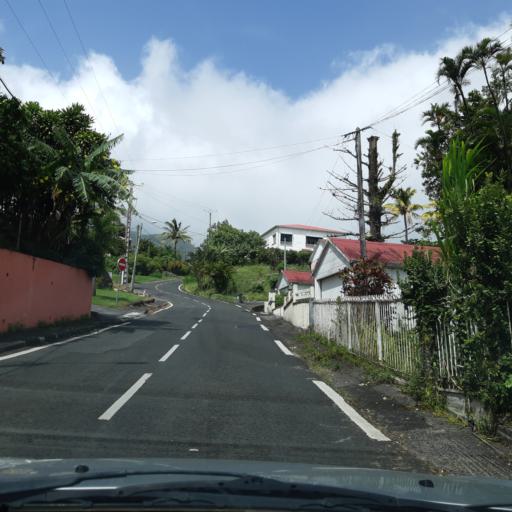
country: GP
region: Guadeloupe
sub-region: Guadeloupe
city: Saint-Claude
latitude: 16.0291
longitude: -61.6910
